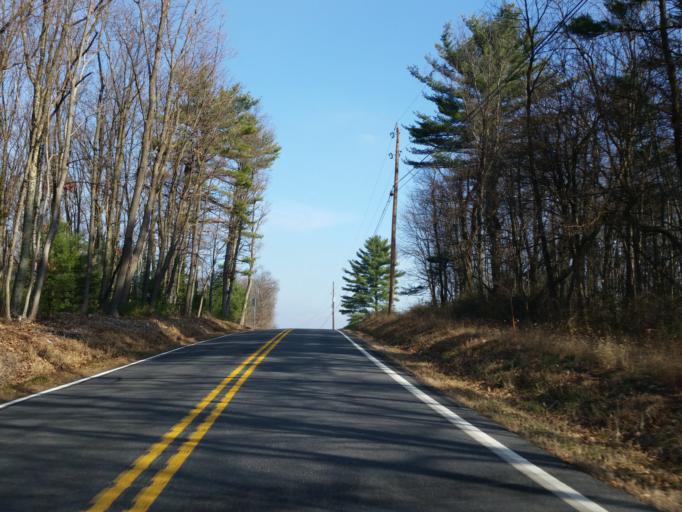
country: US
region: Pennsylvania
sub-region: Dauphin County
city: Williamstown
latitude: 40.4619
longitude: -76.5930
